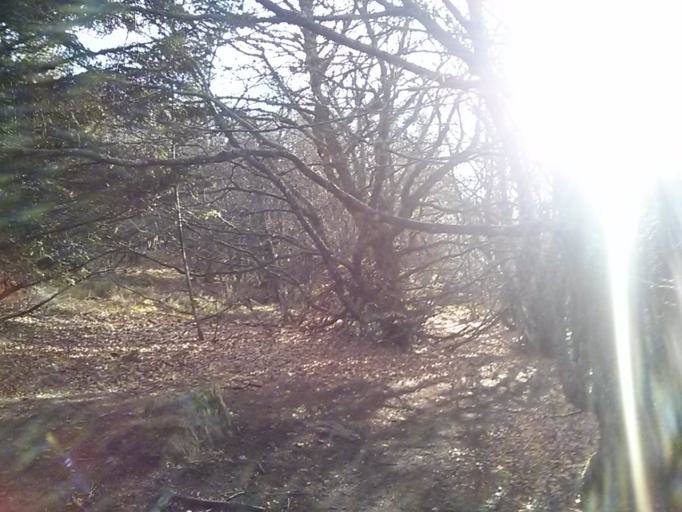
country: FR
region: Rhone-Alpes
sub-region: Departement de la Loire
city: Saint-Julien-Molin-Molette
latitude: 45.3812
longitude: 4.5780
